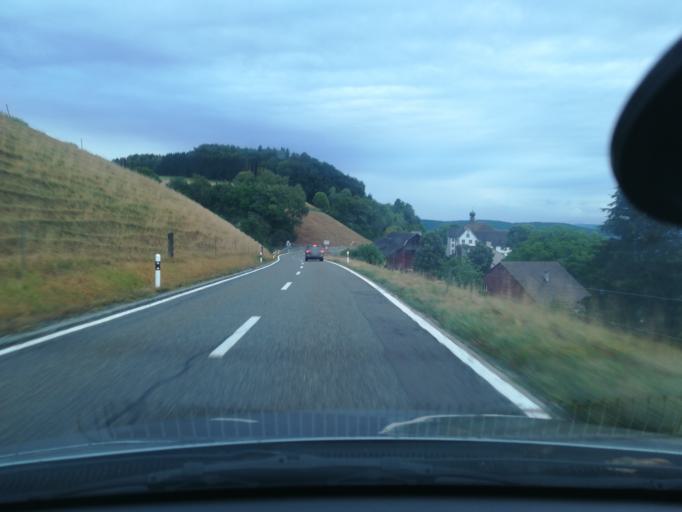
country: CH
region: Thurgau
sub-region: Frauenfeld District
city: Huttwilen
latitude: 47.6131
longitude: 8.8874
